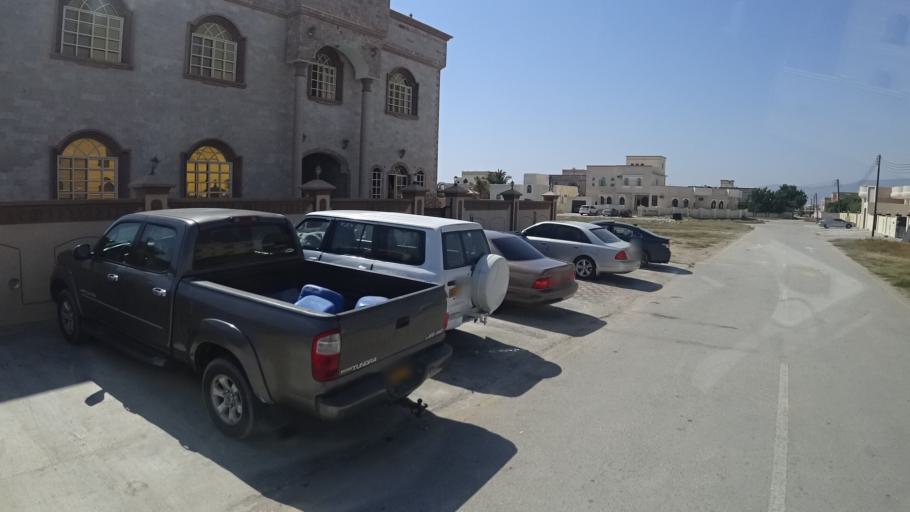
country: OM
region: Zufar
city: Salalah
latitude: 16.9841
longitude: 54.7103
